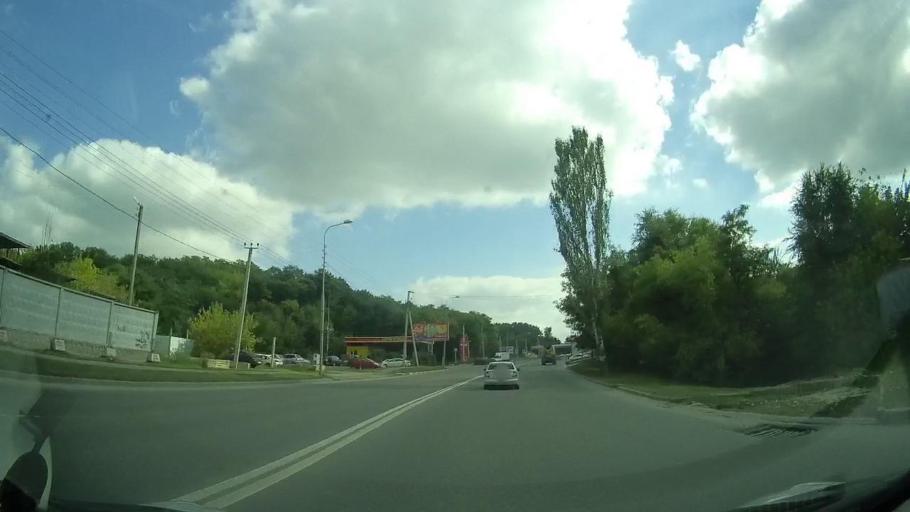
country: RU
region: Rostov
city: Imeni Chkalova
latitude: 47.2573
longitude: 39.7932
